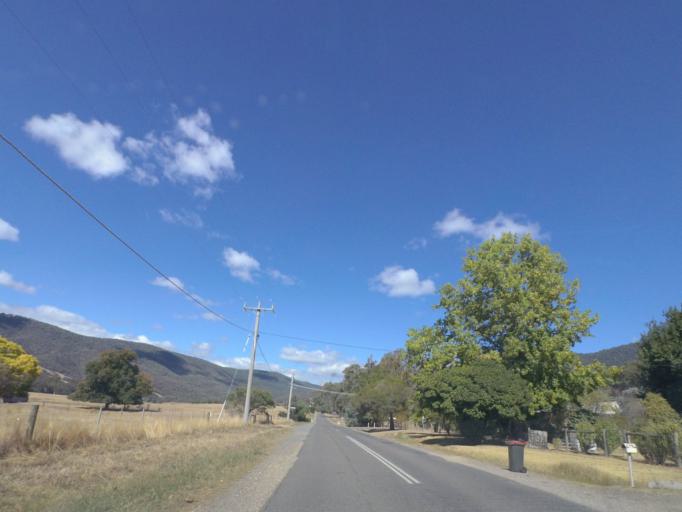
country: AU
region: Victoria
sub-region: Murrindindi
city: Alexandra
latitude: -37.2936
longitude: 145.8201
